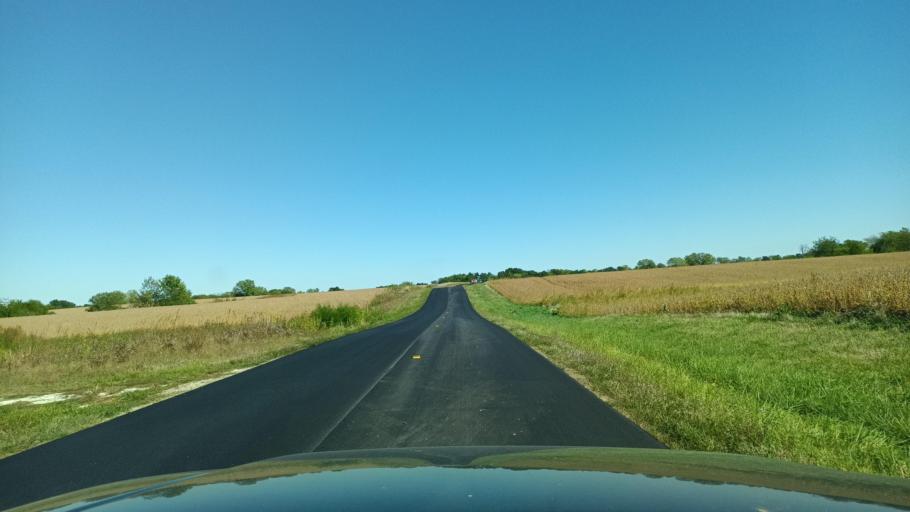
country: US
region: Missouri
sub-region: Macon County
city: La Plata
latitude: 39.9273
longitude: -92.5457
